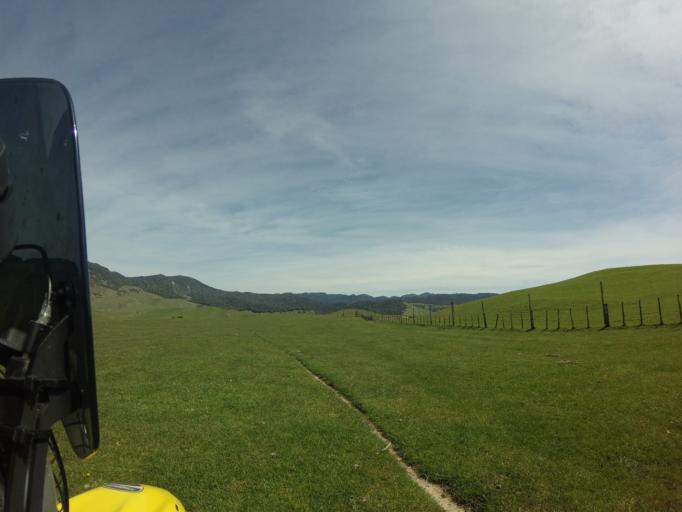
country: NZ
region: Bay of Plenty
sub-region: Opotiki District
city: Opotiki
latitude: -38.4724
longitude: 177.3775
